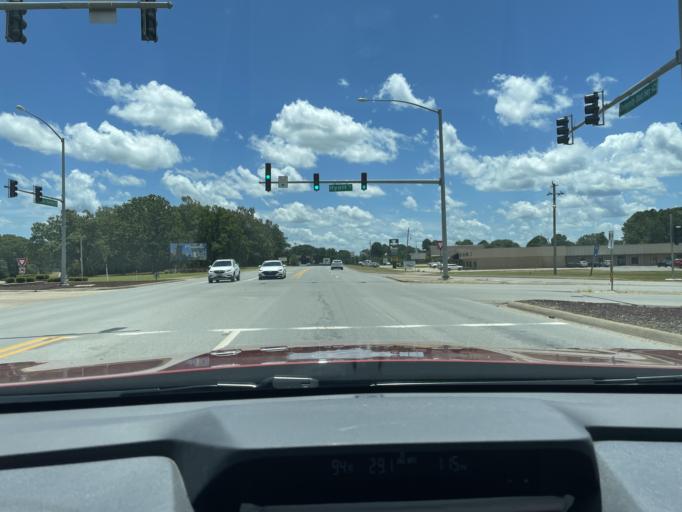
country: US
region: Arkansas
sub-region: Drew County
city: Monticello
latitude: 33.6486
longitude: -91.8016
